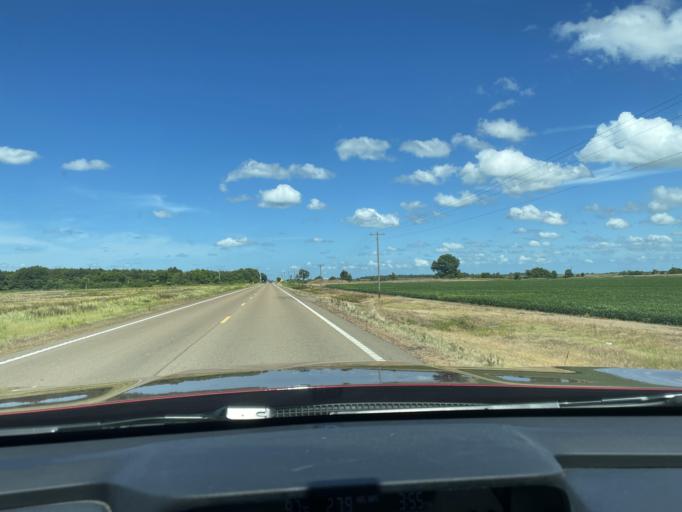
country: US
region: Mississippi
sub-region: Humphreys County
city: Belzoni
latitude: 33.1826
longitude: -90.6372
